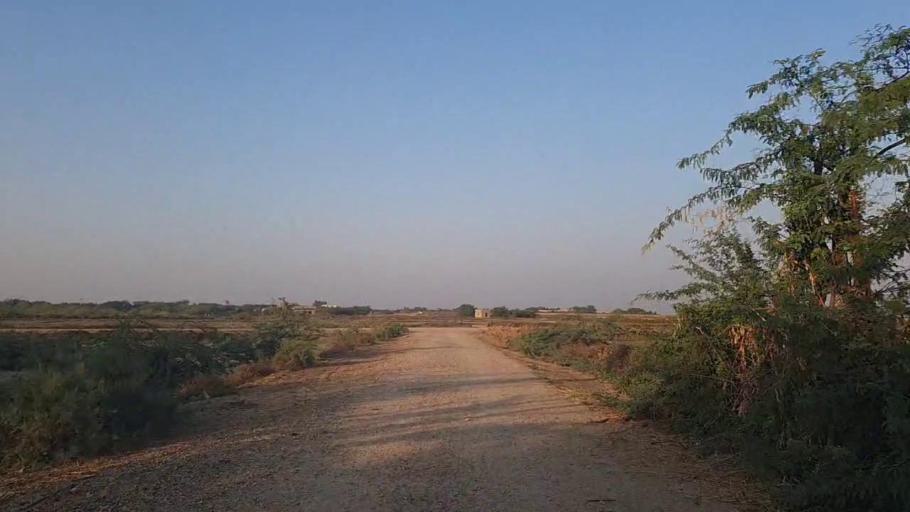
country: PK
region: Sindh
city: Thatta
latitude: 24.6808
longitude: 67.9494
